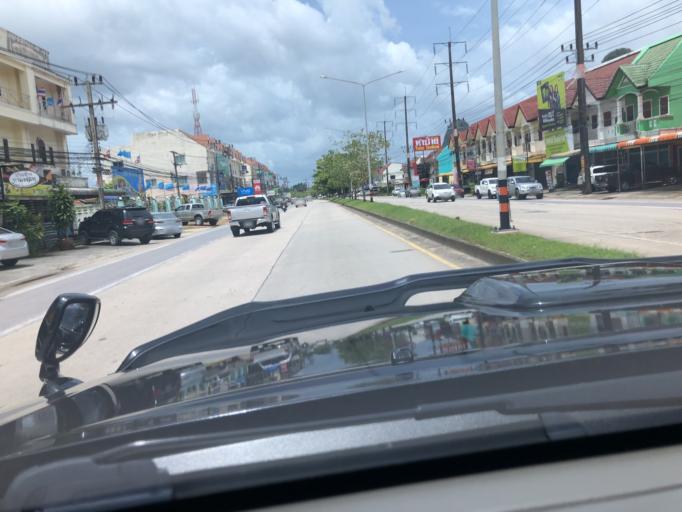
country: TH
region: Phangnga
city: Phang Nga
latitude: 8.4446
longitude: 98.5295
